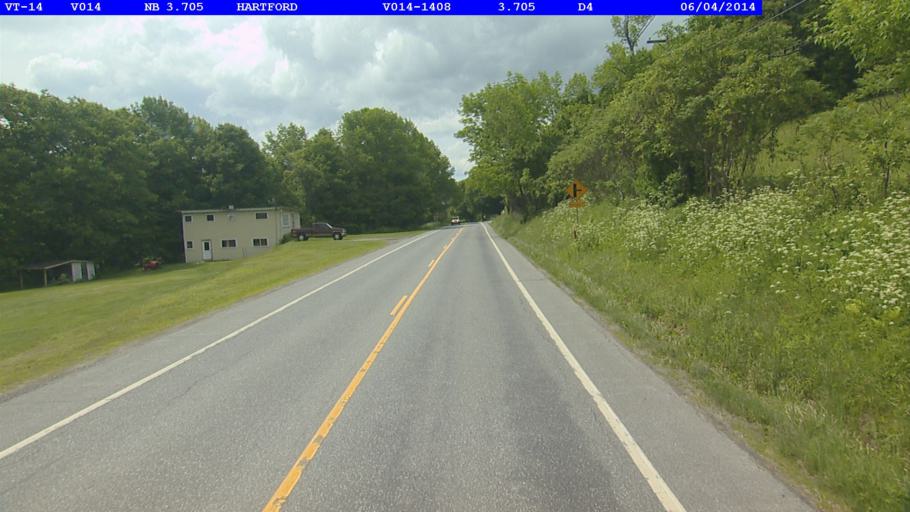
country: US
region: Vermont
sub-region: Windsor County
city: White River Junction
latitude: 43.6751
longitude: -72.3843
